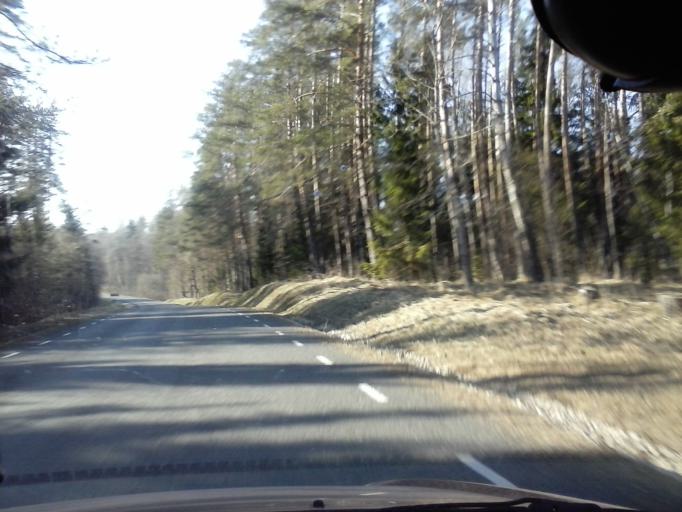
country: EE
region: Tartu
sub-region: UElenurme vald
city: Ulenurme
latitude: 58.1534
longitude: 26.8704
